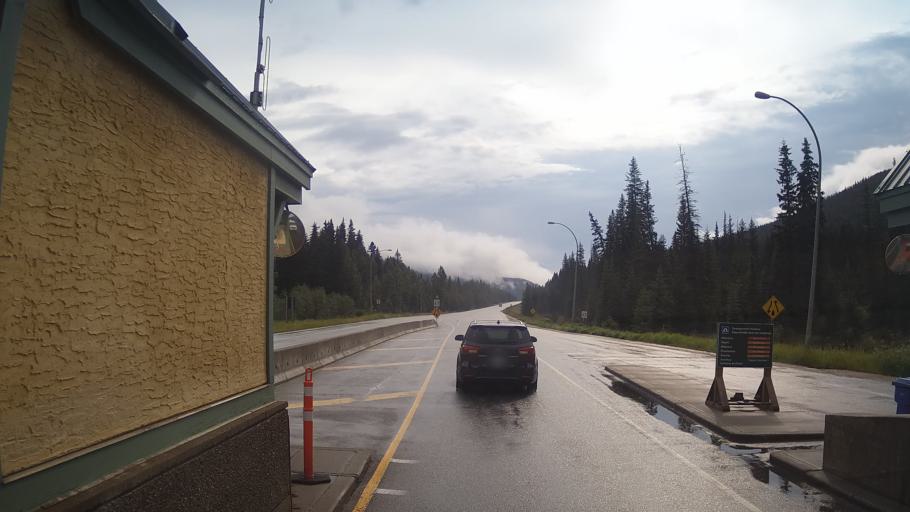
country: CA
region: Alberta
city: Jasper Park Lodge
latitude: 52.8831
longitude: -118.3934
